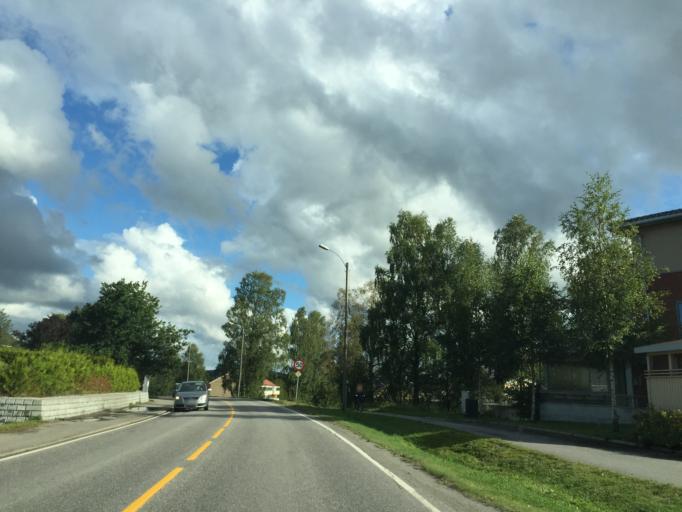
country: NO
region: Hedmark
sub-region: Kongsvinger
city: Kongsvinger
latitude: 60.1961
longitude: 12.0000
